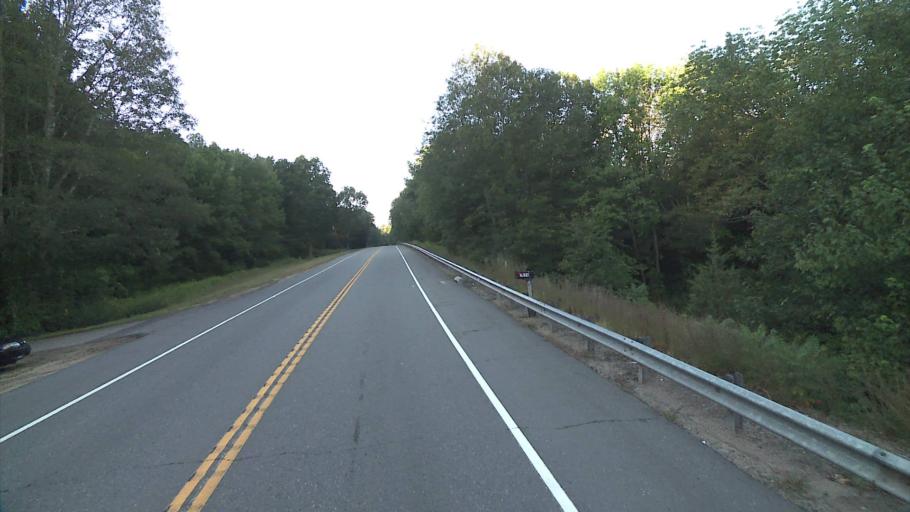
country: US
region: Connecticut
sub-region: Tolland County
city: South Coventry
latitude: 41.8310
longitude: -72.3069
